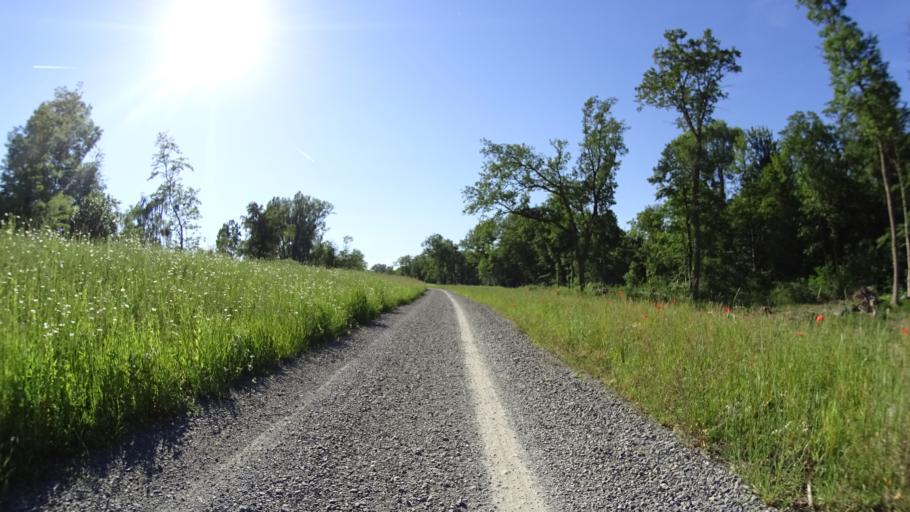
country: DE
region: Baden-Wuerttemberg
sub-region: Karlsruhe Region
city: Eggenstein-Leopoldshafen
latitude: 49.1037
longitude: 8.3790
